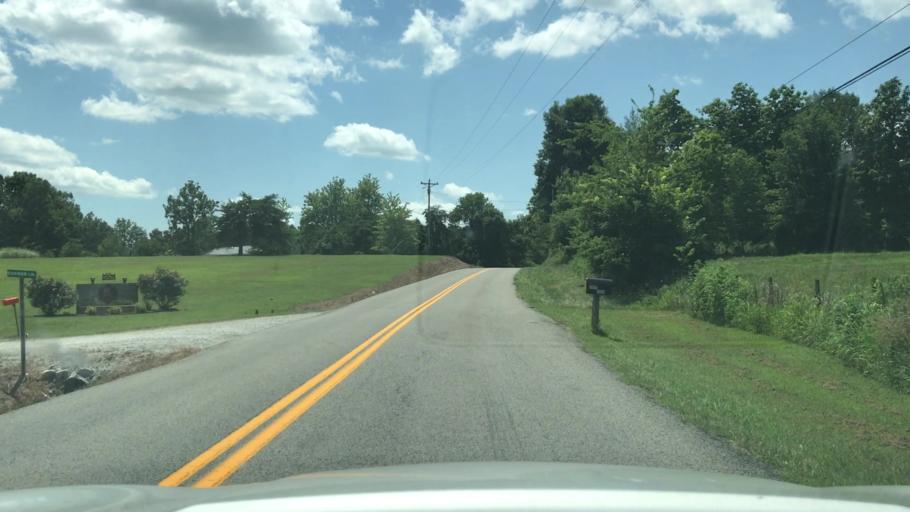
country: US
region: Kentucky
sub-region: Christian County
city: Hopkinsville
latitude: 36.9729
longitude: -87.3699
